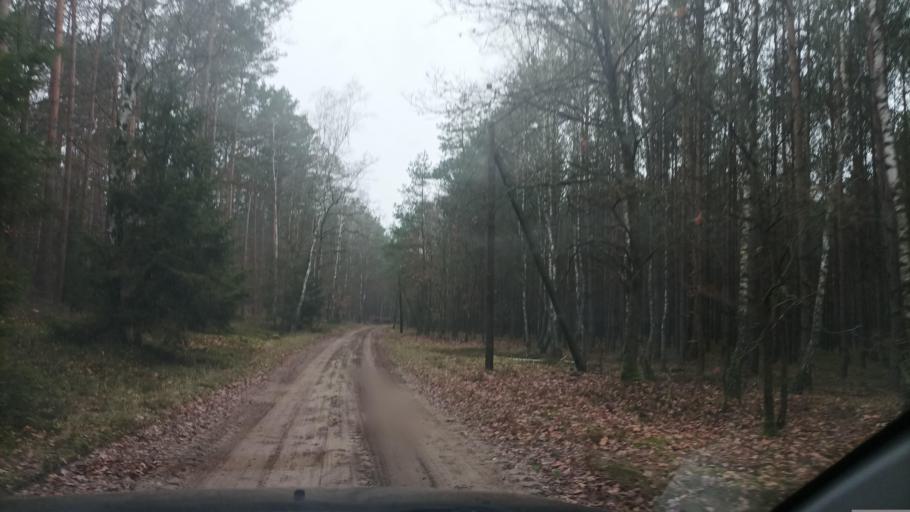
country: PL
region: Greater Poland Voivodeship
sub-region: Powiat czarnkowsko-trzcianecki
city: Polajewo
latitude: 52.7499
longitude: 16.7831
